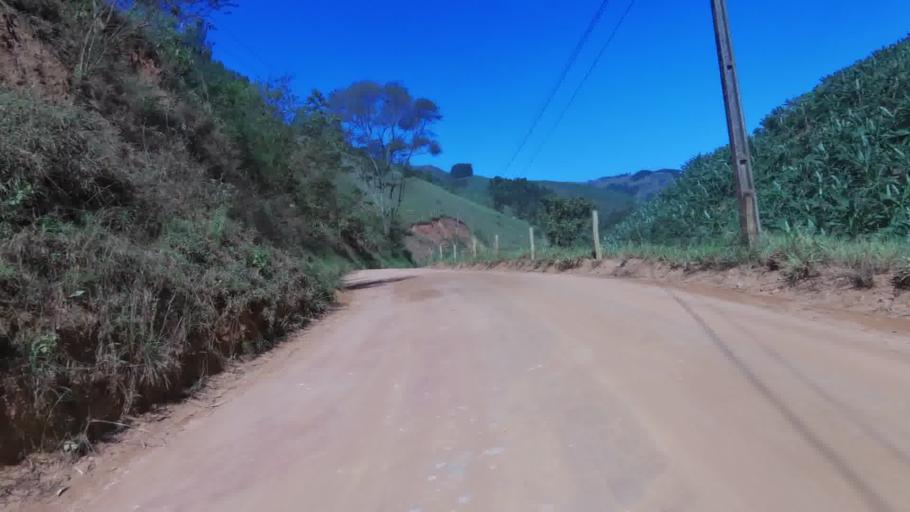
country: BR
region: Espirito Santo
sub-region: Alfredo Chaves
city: Alfredo Chaves
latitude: -20.6479
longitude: -40.8022
